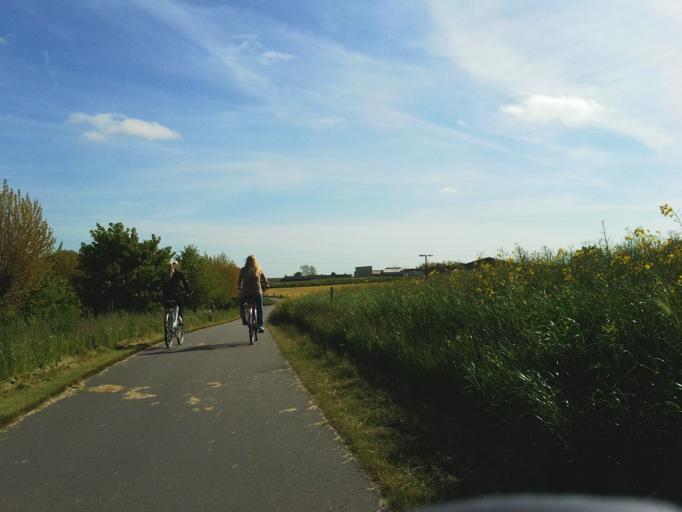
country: DE
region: Mecklenburg-Vorpommern
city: Schwaan
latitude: 53.9783
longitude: 12.1018
